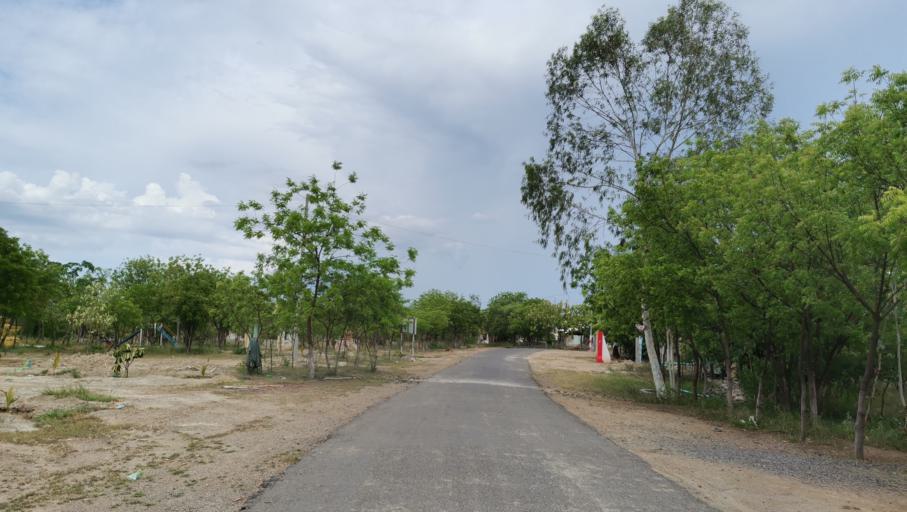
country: MM
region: Mandalay
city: Myingyan
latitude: 21.8251
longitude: 95.3946
